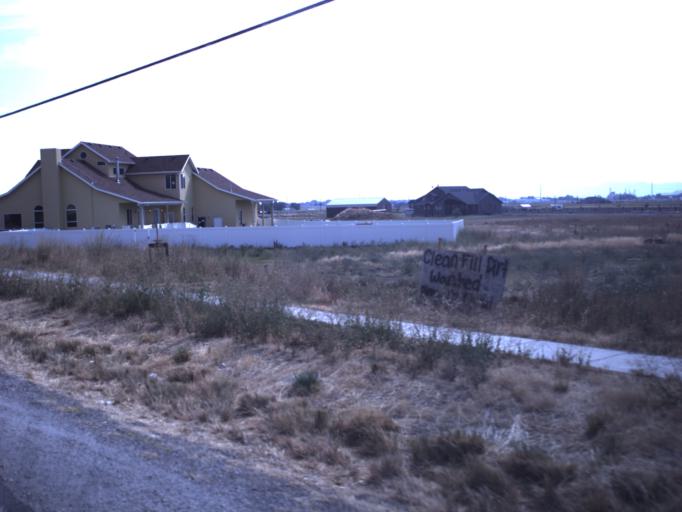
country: US
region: Utah
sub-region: Box Elder County
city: Honeyville
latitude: 41.6531
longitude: -112.0849
